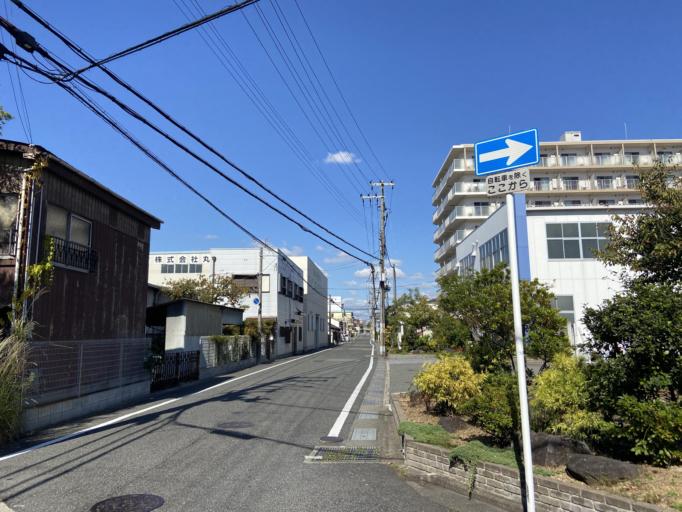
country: JP
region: Osaka
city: Sakai
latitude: 34.5502
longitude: 135.4628
